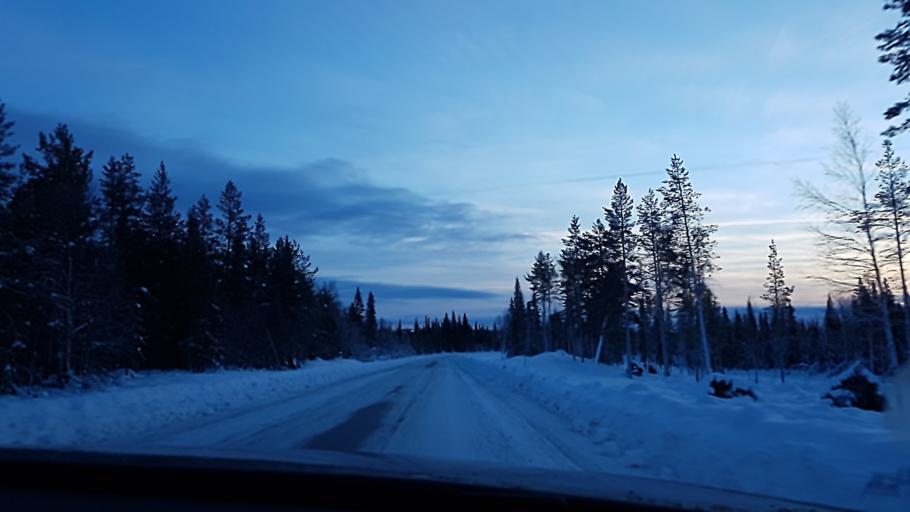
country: SE
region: Norrbotten
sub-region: Jokkmokks Kommun
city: Jokkmokk
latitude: 66.1015
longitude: 20.0627
